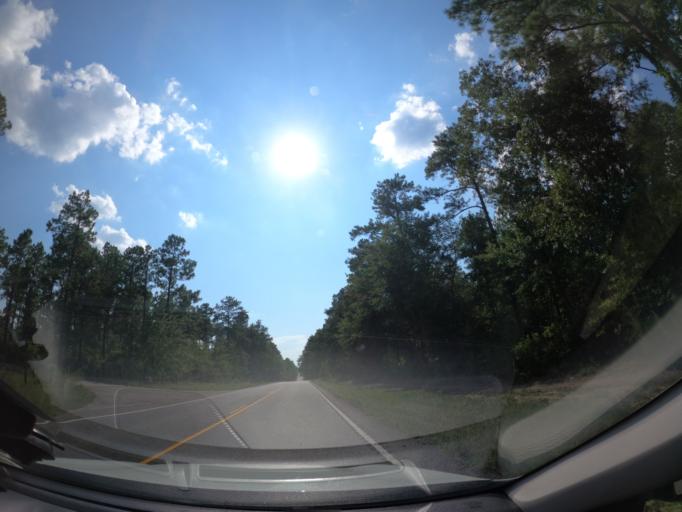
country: US
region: South Carolina
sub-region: Aiken County
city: New Ellenton
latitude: 33.3896
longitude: -81.5756
